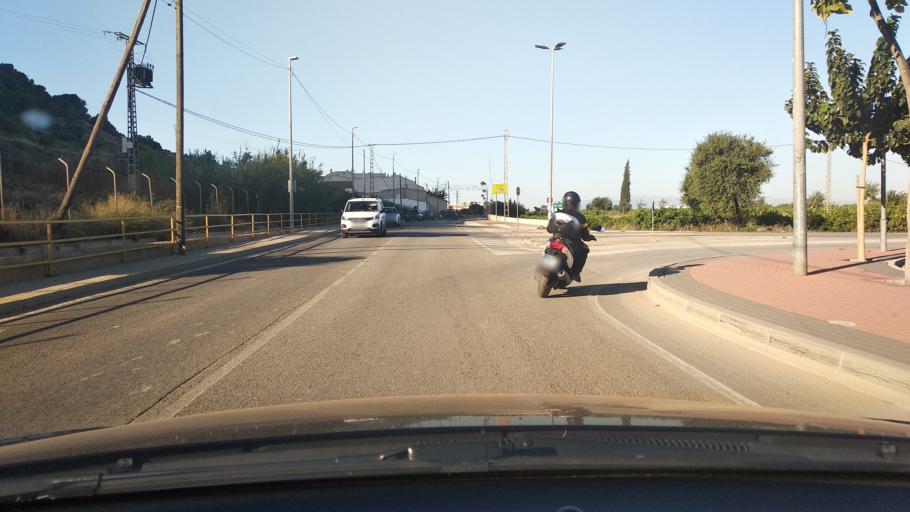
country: ES
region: Murcia
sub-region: Murcia
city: Beniel
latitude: 37.9876
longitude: -1.0429
